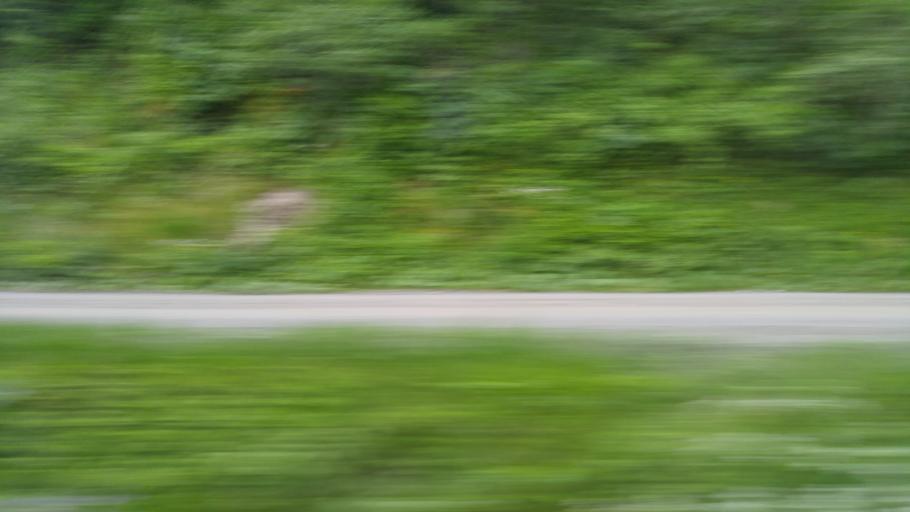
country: NO
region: Nord-Trondelag
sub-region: Meraker
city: Meraker
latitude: 63.4569
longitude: 11.4426
